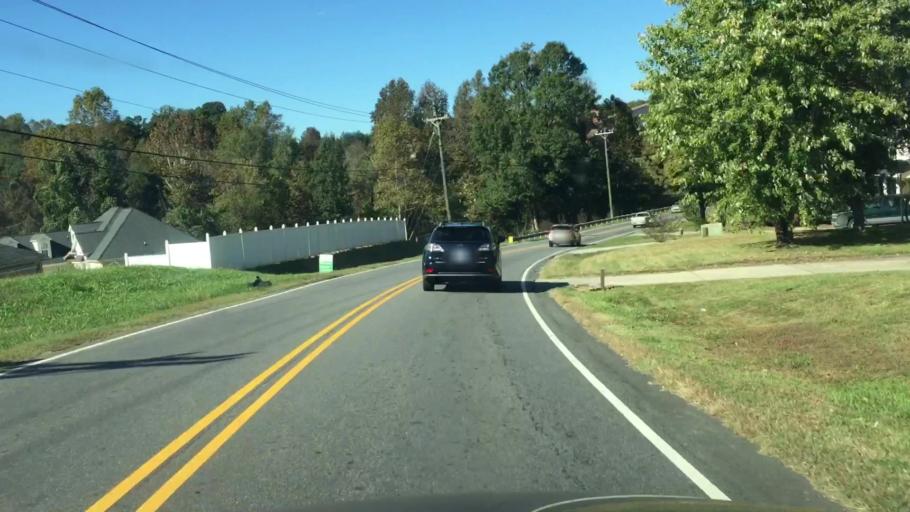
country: US
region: North Carolina
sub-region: Iredell County
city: Mooresville
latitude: 35.5769
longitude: -80.8465
